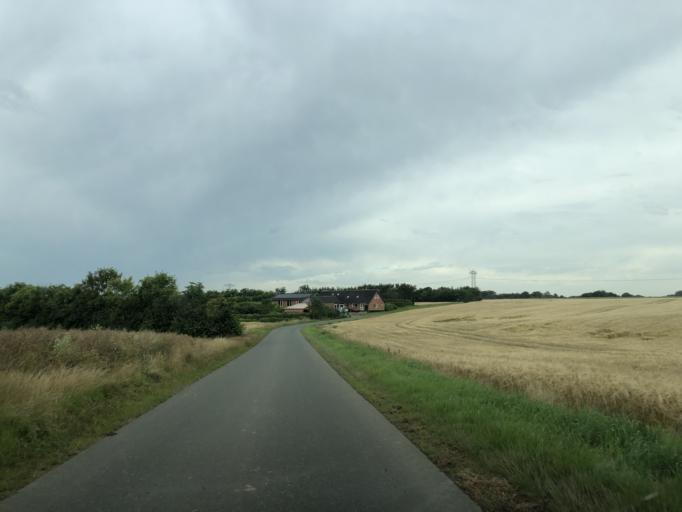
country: DK
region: Central Jutland
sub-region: Holstebro Kommune
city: Holstebro
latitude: 56.3968
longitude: 8.5932
